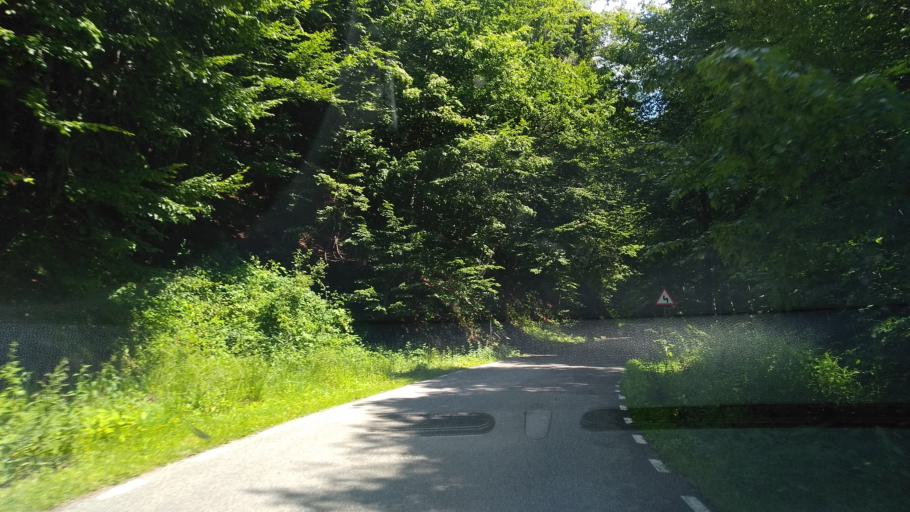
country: RO
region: Hunedoara
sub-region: Comuna Orastioara de Sus
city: Orastioara de Sus
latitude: 45.6219
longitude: 23.2712
